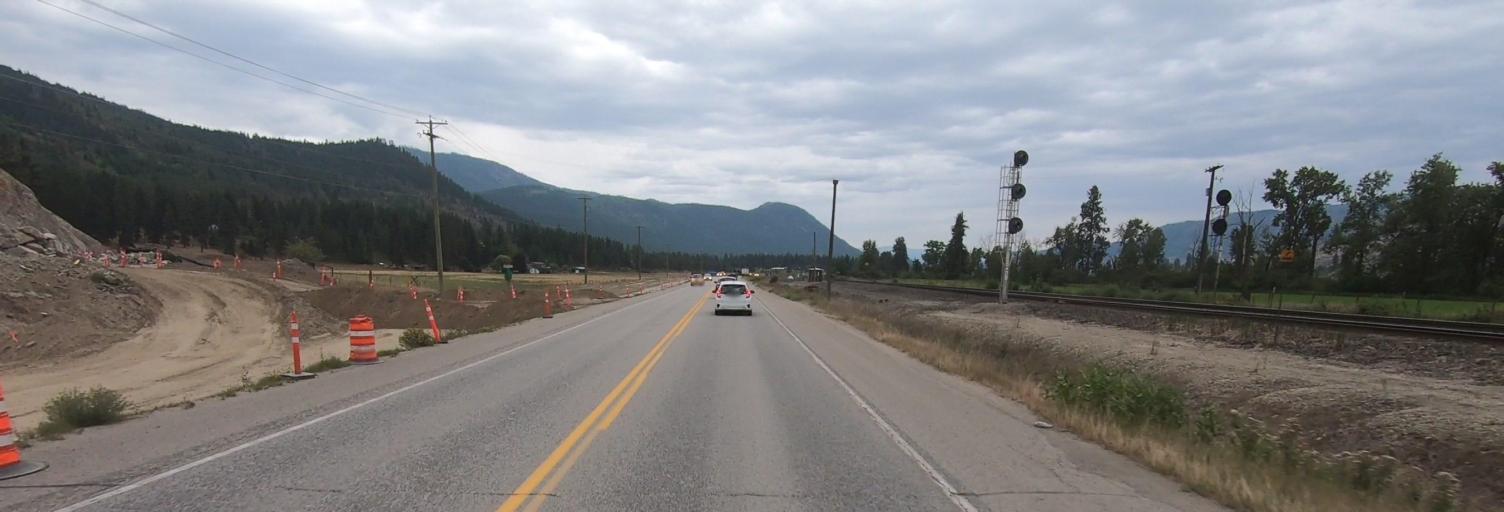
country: CA
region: British Columbia
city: Chase
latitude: 50.7841
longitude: -119.7121
